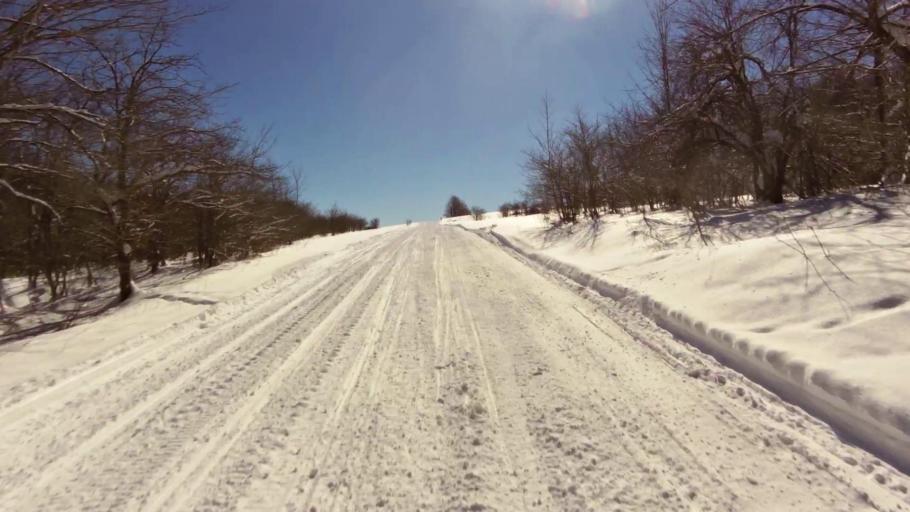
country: US
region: New York
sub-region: Chautauqua County
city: Mayville
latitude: 42.2239
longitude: -79.5198
